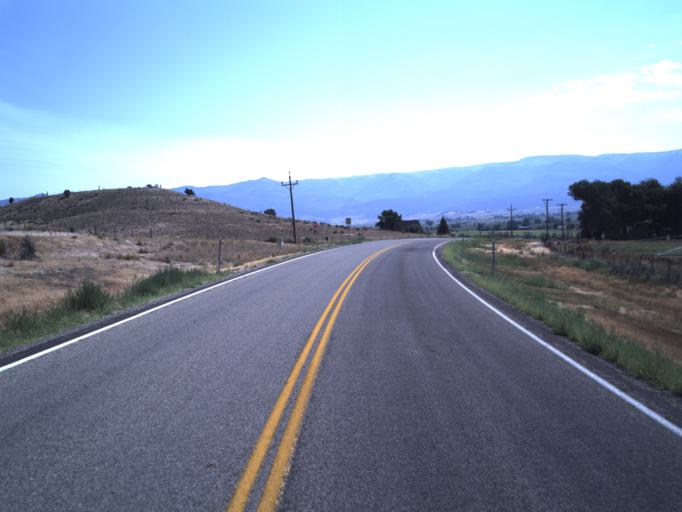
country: US
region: Utah
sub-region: Sanpete County
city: Moroni
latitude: 39.5462
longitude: -111.5261
